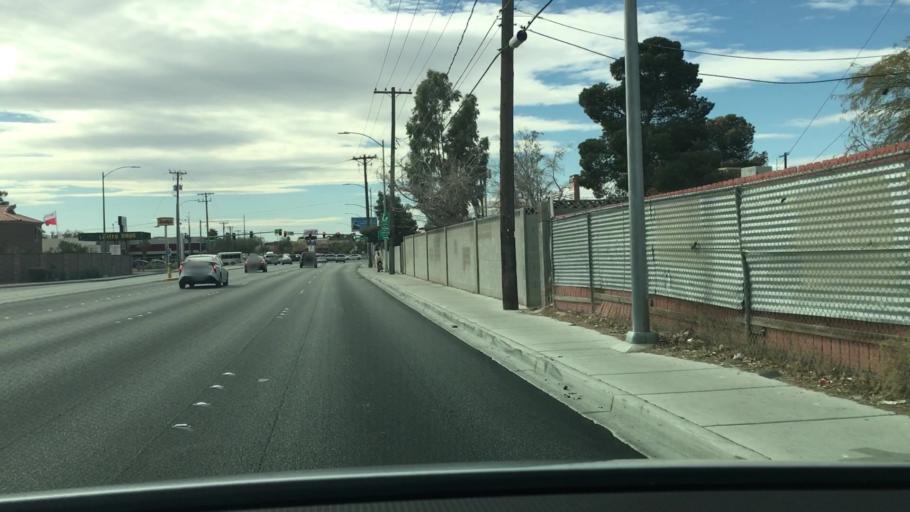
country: US
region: Nevada
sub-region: Clark County
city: Spring Valley
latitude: 36.1610
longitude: -115.2240
